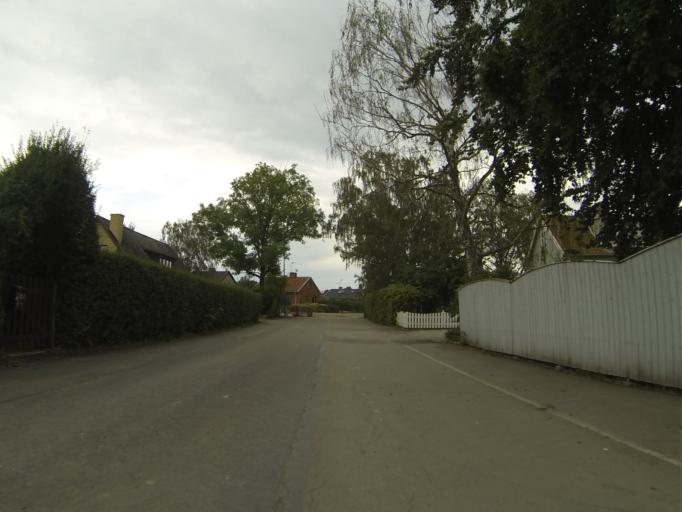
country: SE
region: Skane
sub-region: Staffanstorps Kommun
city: Staffanstorp
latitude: 55.6495
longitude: 13.2073
